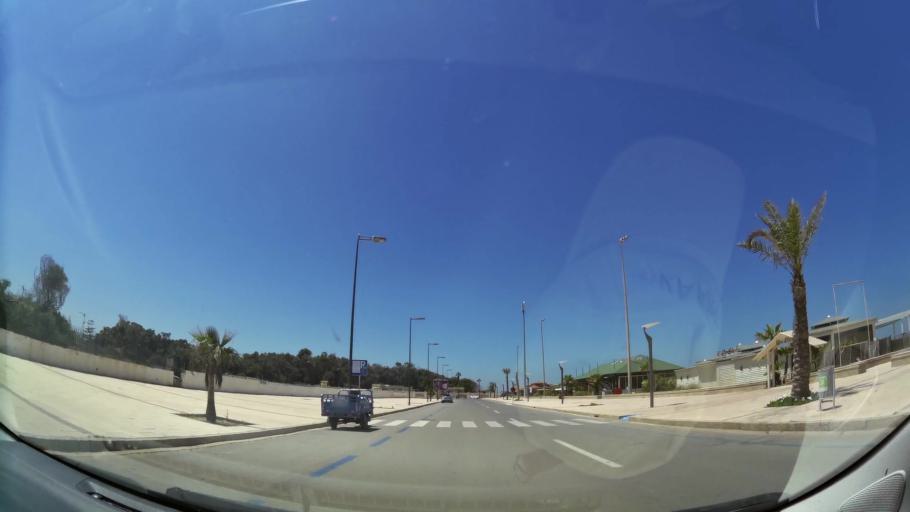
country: MA
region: Oriental
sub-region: Berkane-Taourirt
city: Madagh
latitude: 35.0881
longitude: -2.2320
